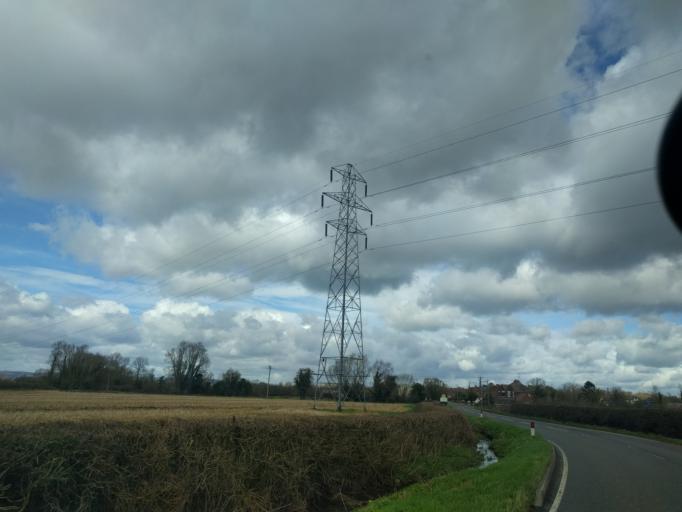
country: GB
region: England
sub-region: Gloucestershire
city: Stonehouse
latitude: 51.7375
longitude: -2.3201
